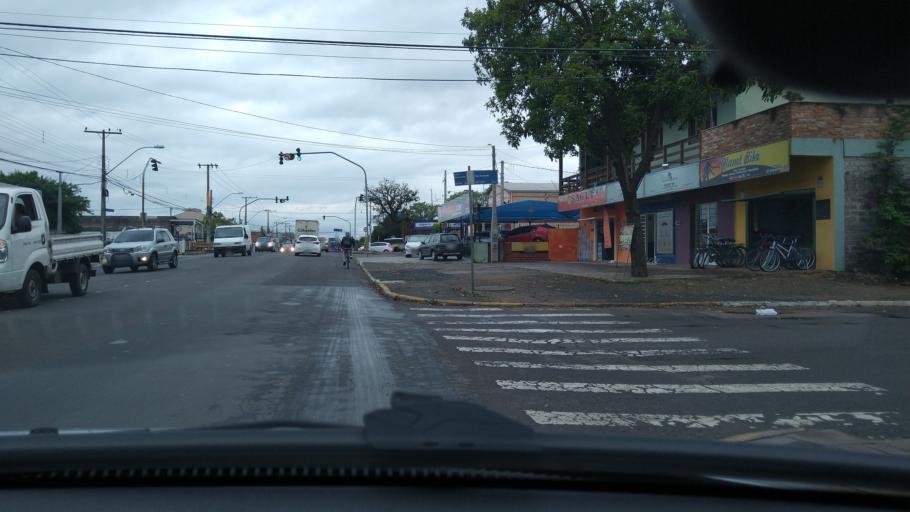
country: BR
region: Rio Grande do Sul
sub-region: Canoas
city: Canoas
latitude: -29.9023
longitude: -51.2009
